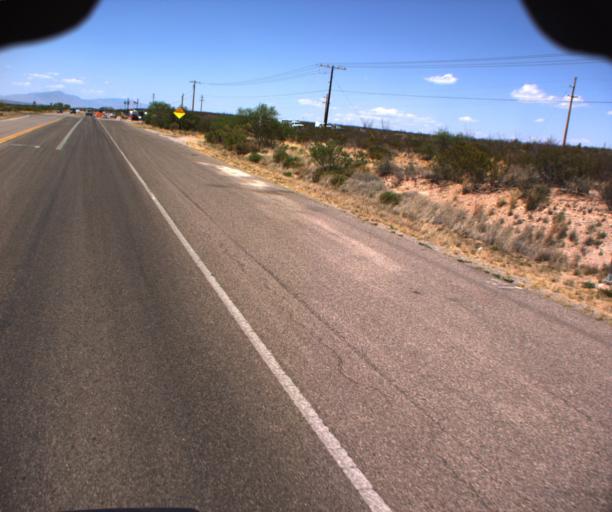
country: US
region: Arizona
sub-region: Cochise County
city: Tombstone
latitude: 31.7477
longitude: -110.0962
